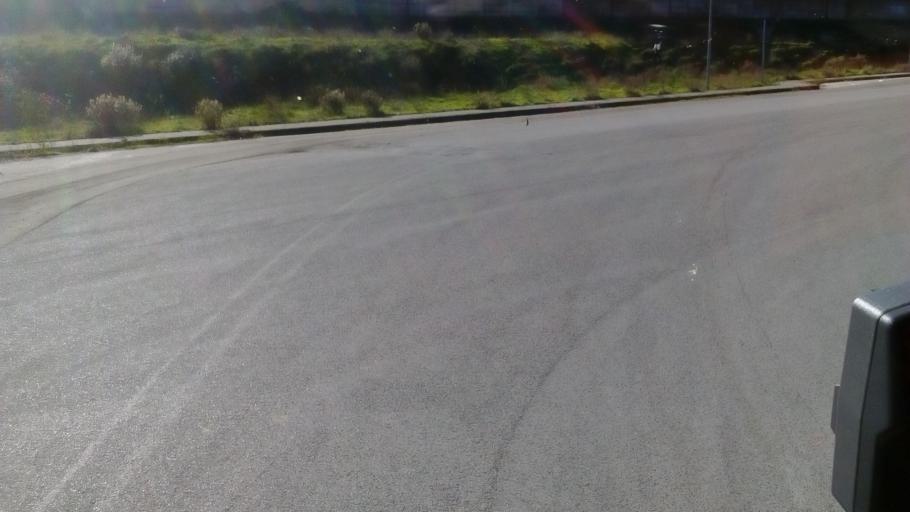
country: IT
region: Basilicate
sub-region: Provincia di Potenza
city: Melfi
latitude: 41.0778
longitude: 15.6722
